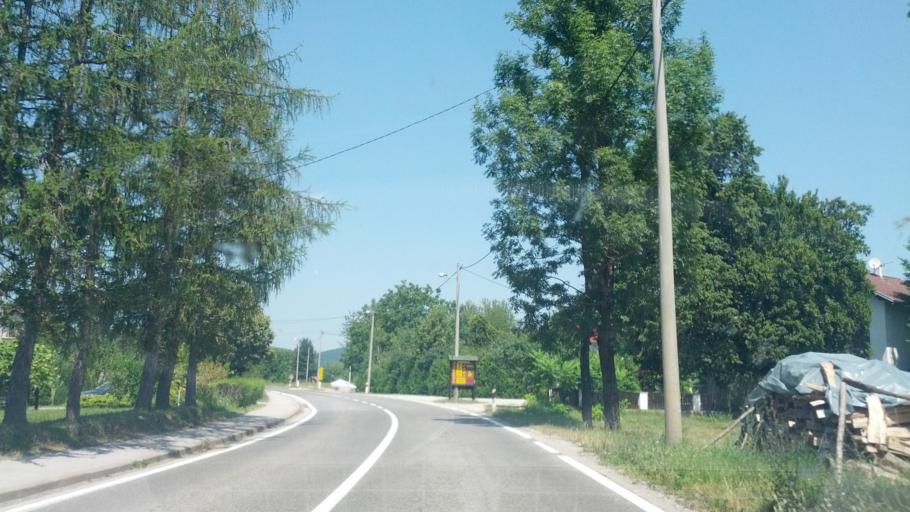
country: HR
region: Licko-Senjska
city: Jezerce
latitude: 44.9634
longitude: 15.6549
